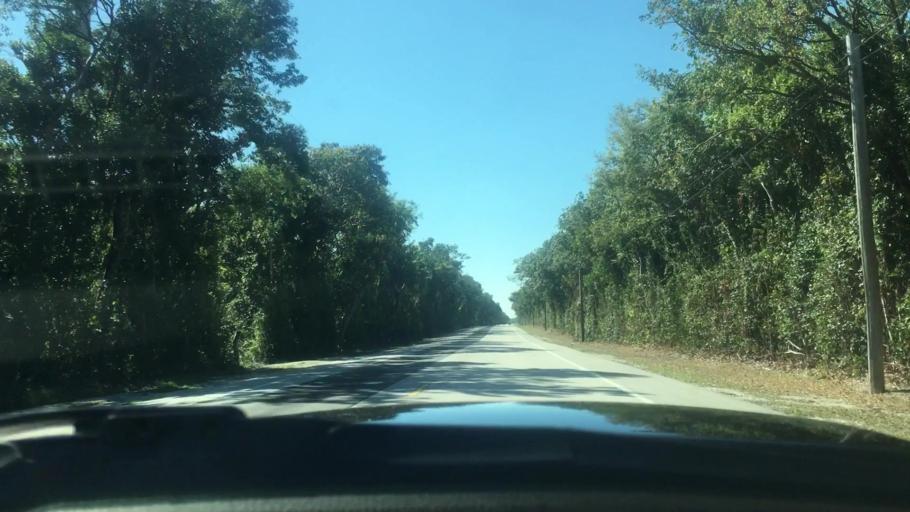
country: US
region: Florida
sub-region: Monroe County
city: North Key Largo
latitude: 25.2447
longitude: -80.3198
